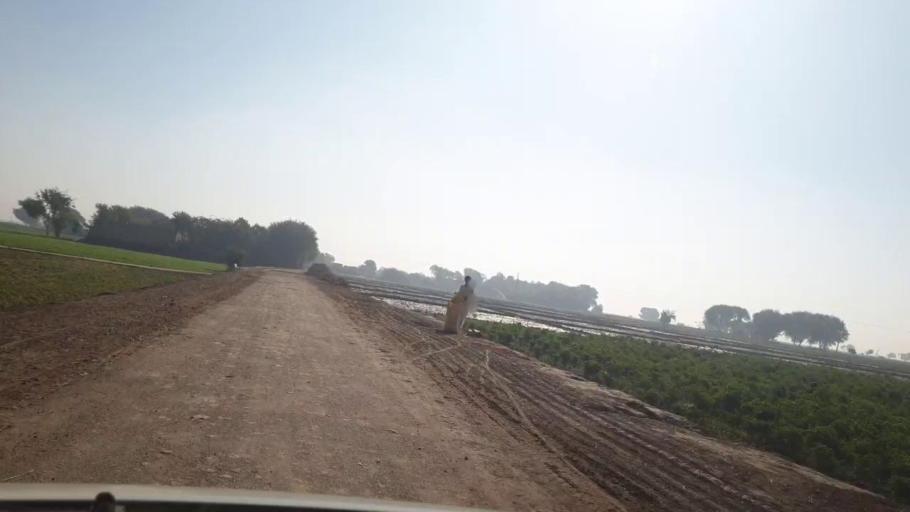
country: PK
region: Sindh
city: Dadu
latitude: 26.6380
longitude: 67.8331
